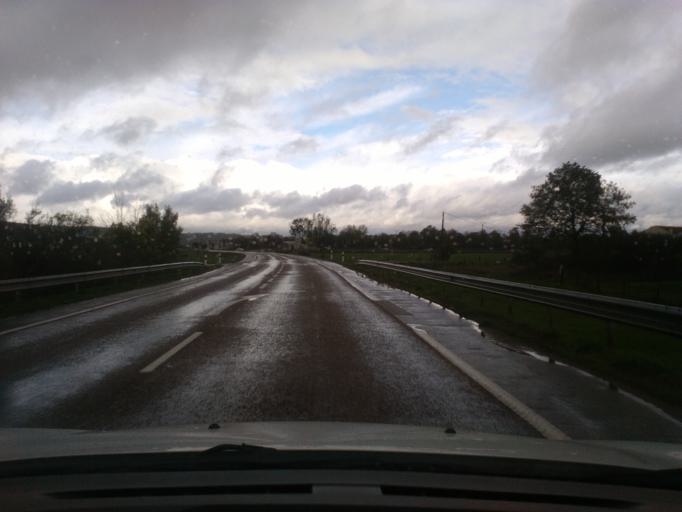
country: FR
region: Lorraine
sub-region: Departement des Vosges
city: Charmes
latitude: 48.3739
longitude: 6.2729
